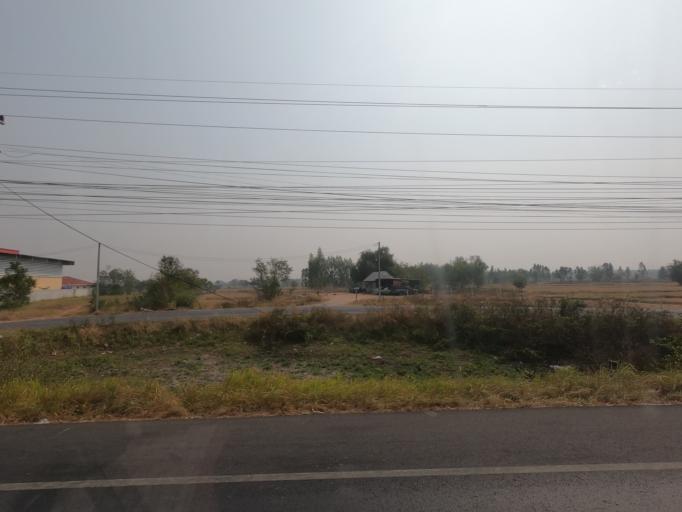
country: TH
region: Khon Kaen
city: Phon
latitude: 15.7554
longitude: 102.6048
